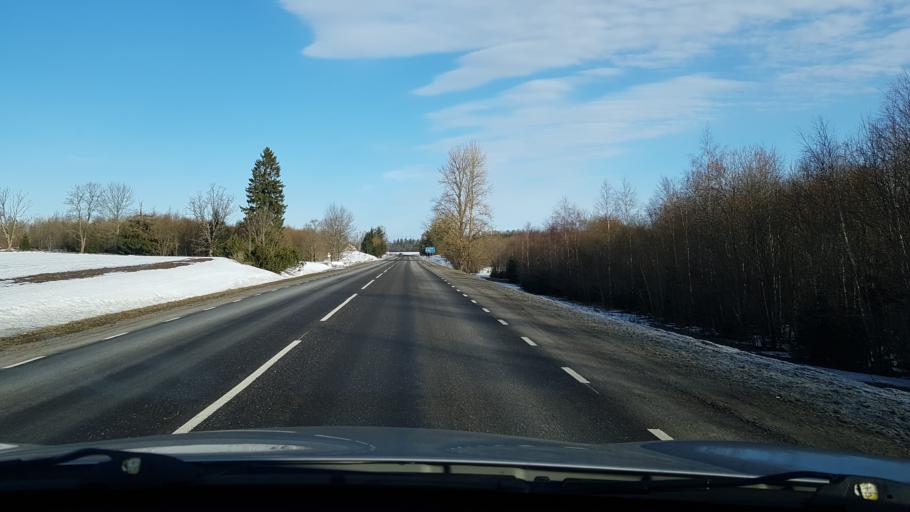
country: EE
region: Viljandimaa
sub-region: Viljandi linn
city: Viljandi
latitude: 58.4172
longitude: 25.5966
